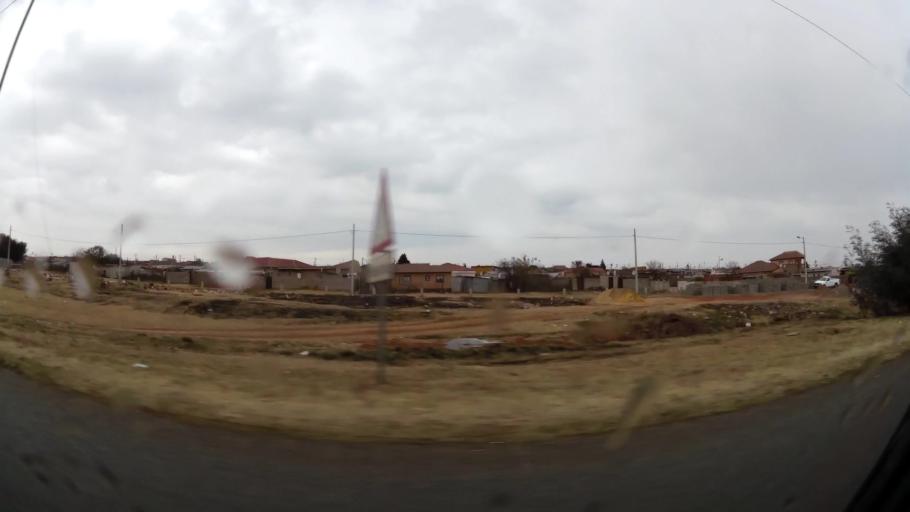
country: ZA
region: Gauteng
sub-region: City of Johannesburg Metropolitan Municipality
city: Roodepoort
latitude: -26.1717
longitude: 27.7873
